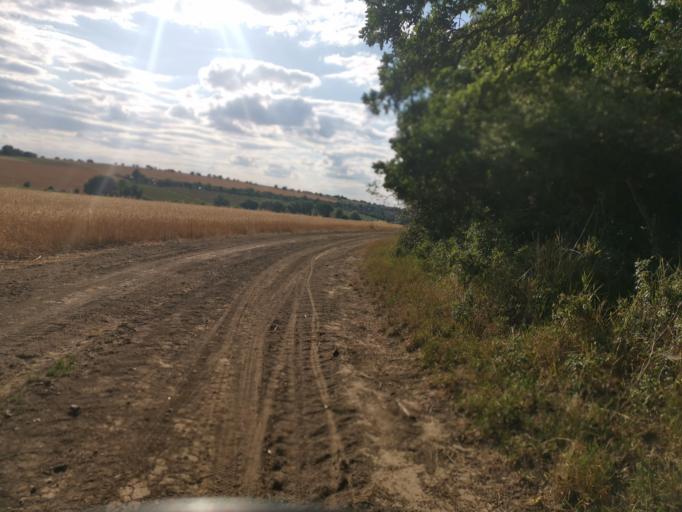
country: SK
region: Trnavsky
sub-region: Okres Skalica
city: Skalica
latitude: 48.8216
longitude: 17.2626
